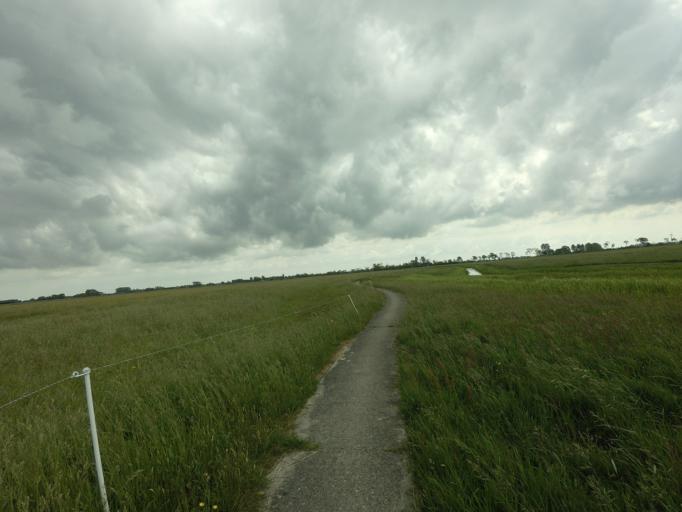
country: NL
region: Friesland
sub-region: Gemeente Littenseradiel
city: Wommels
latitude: 53.1102
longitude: 5.6039
